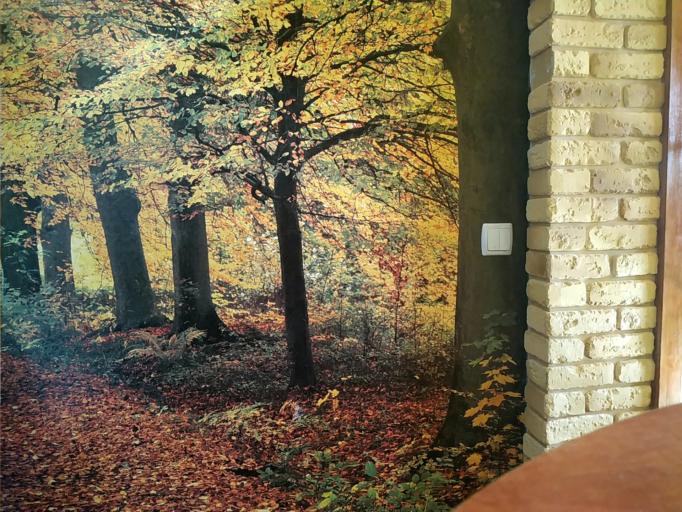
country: RU
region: Jaroslavl
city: Kukoboy
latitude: 58.7969
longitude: 39.7853
